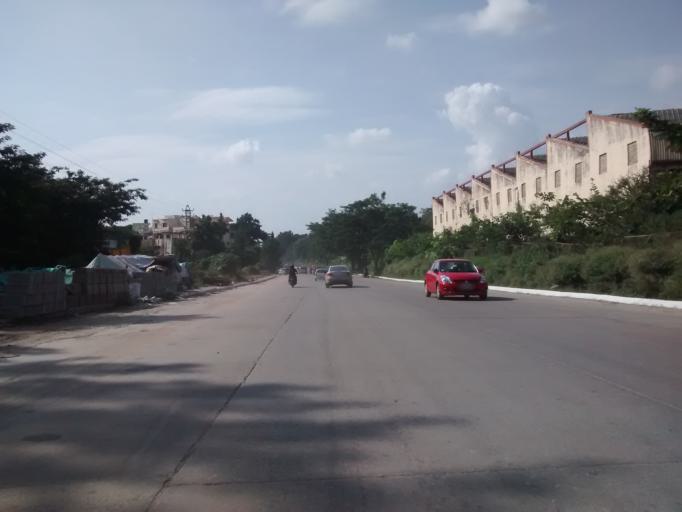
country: IN
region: Karnataka
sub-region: Bangalore Urban
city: Bangalore
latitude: 12.9726
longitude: 77.6580
